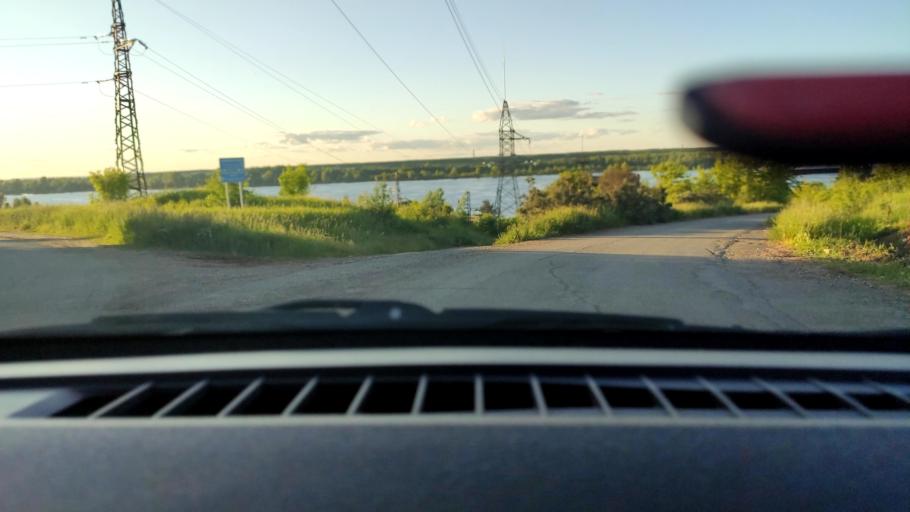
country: RU
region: Perm
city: Kultayevo
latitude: 57.9356
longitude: 55.8648
